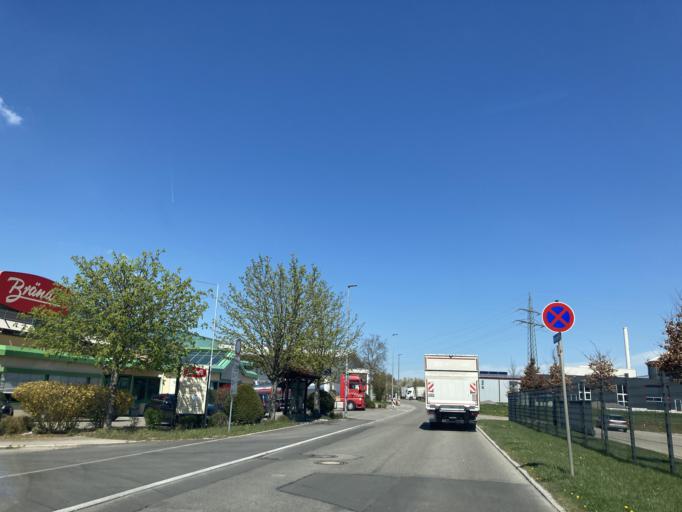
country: DE
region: Baden-Wuerttemberg
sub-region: Karlsruhe Region
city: Empfingen
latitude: 48.3929
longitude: 8.7256
